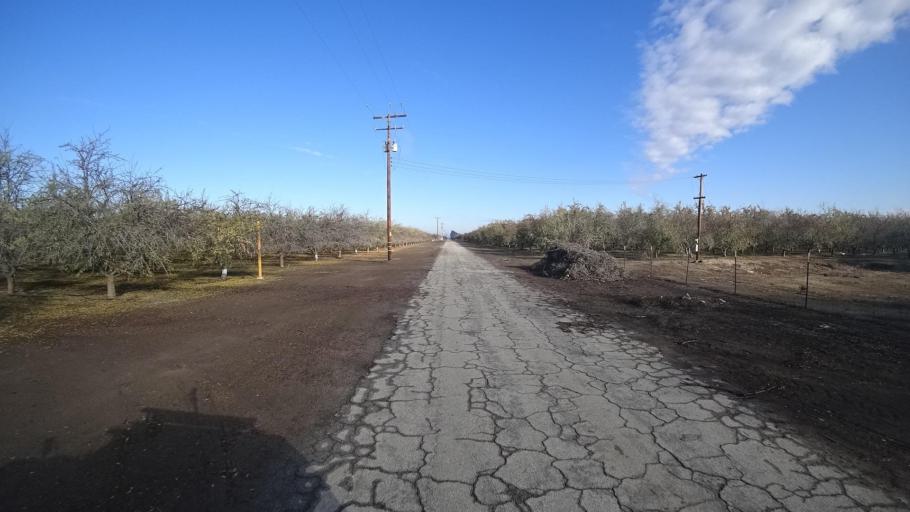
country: US
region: California
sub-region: Kern County
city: Delano
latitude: 35.7084
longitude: -119.3208
